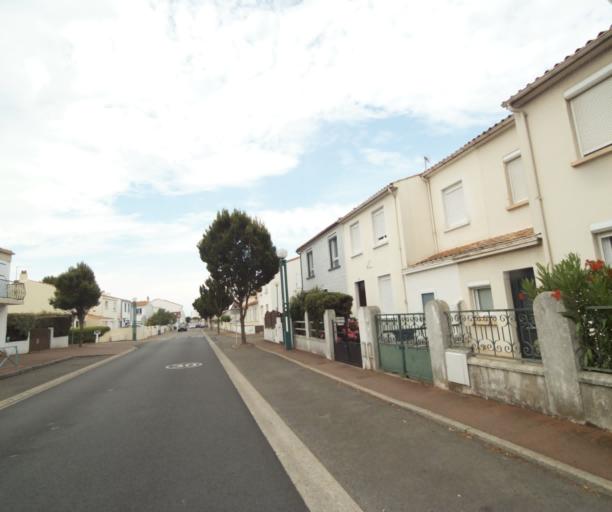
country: FR
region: Pays de la Loire
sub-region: Departement de la Vendee
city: Chateau-d'Olonne
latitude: 46.4945
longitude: -1.7590
